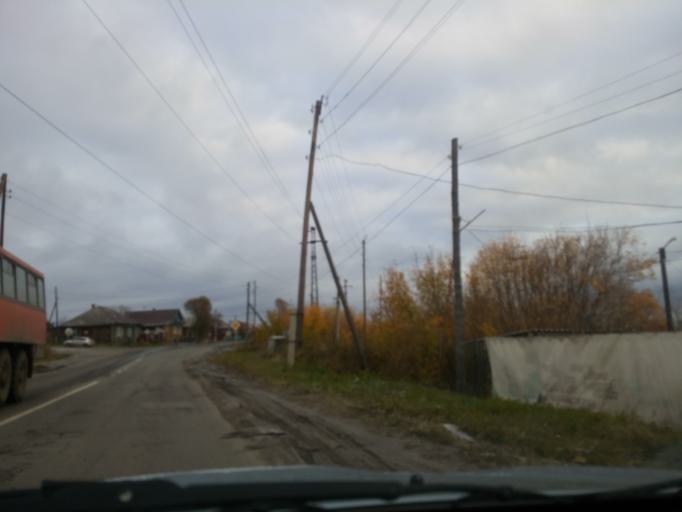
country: RU
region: Sverdlovsk
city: Turinsk
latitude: 58.0313
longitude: 63.7017
